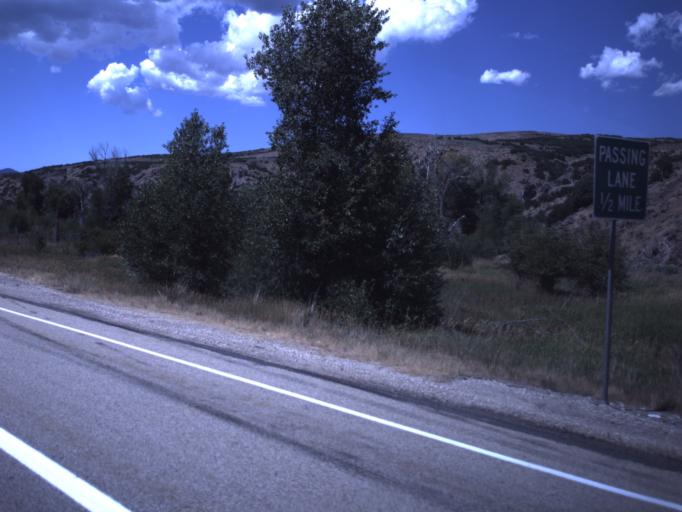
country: US
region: Utah
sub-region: Summit County
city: Francis
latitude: 40.6016
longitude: -111.3305
